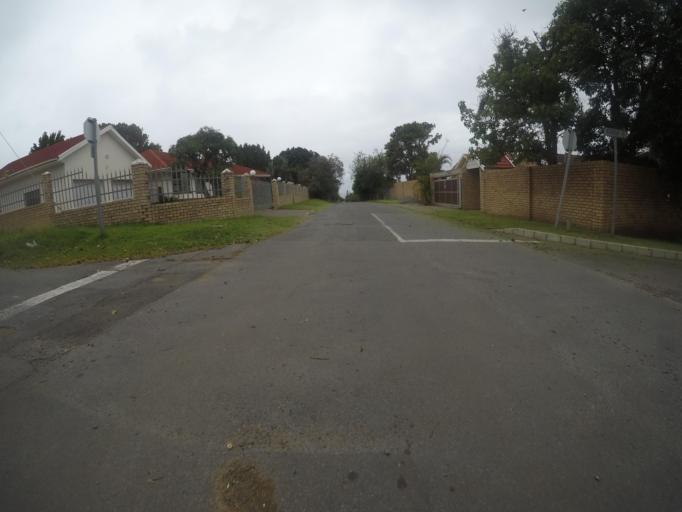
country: ZA
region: Eastern Cape
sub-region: Buffalo City Metropolitan Municipality
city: East London
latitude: -32.9419
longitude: 28.0051
